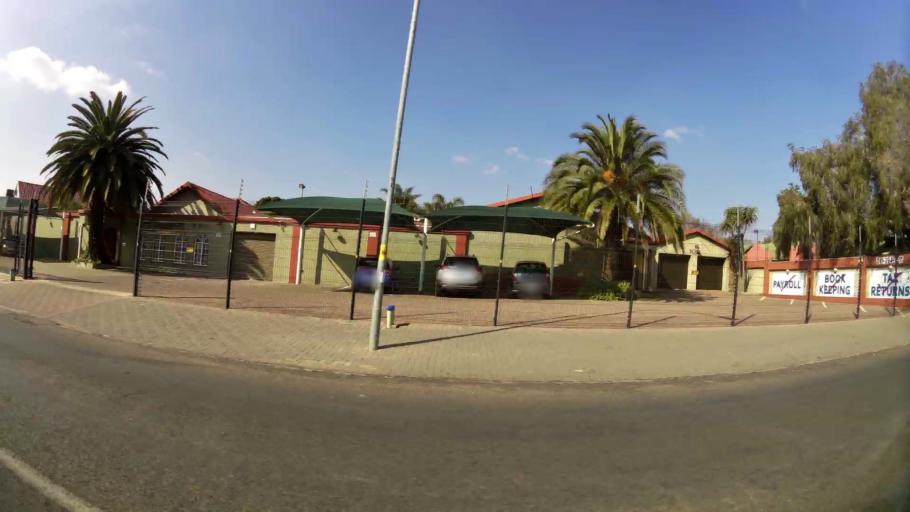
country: ZA
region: Gauteng
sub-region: City of Johannesburg Metropolitan Municipality
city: Modderfontein
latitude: -26.0876
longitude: 28.2388
